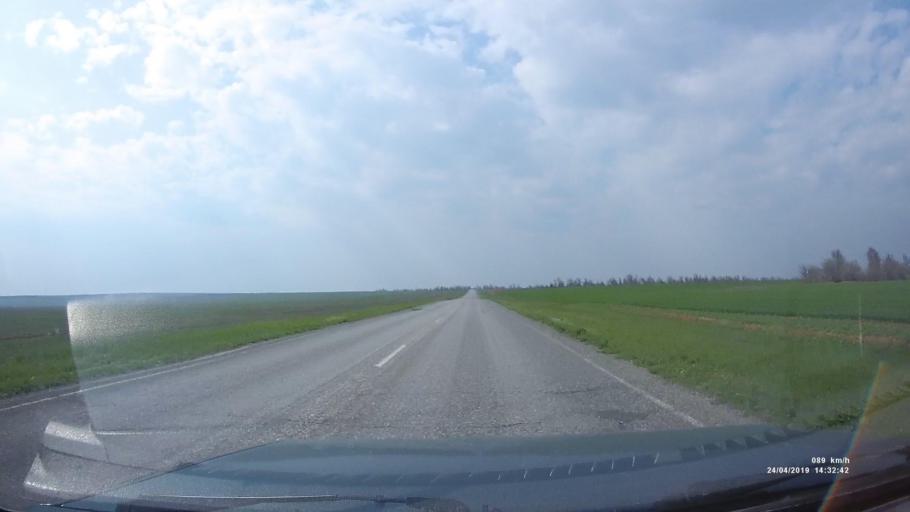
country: RU
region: Kalmykiya
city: Arshan'
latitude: 46.3669
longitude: 43.9649
